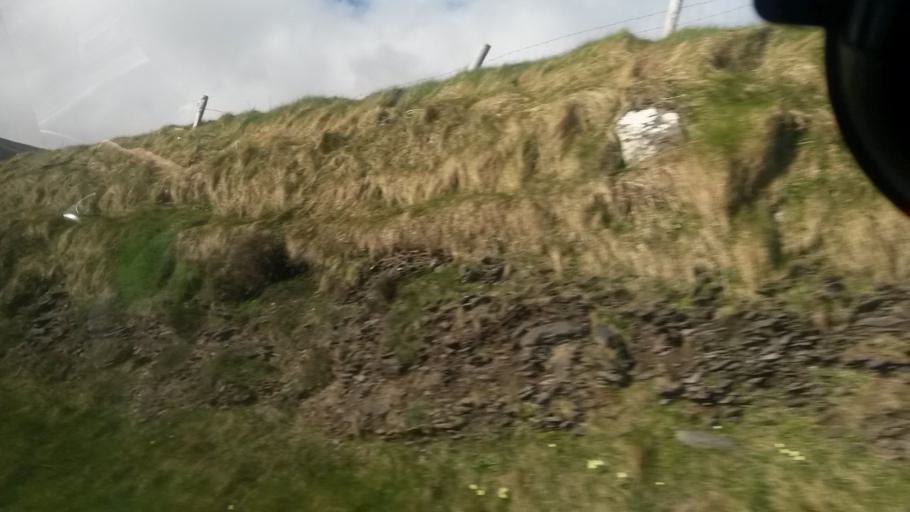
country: IE
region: Munster
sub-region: Ciarrai
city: Dingle
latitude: 52.1002
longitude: -10.4264
